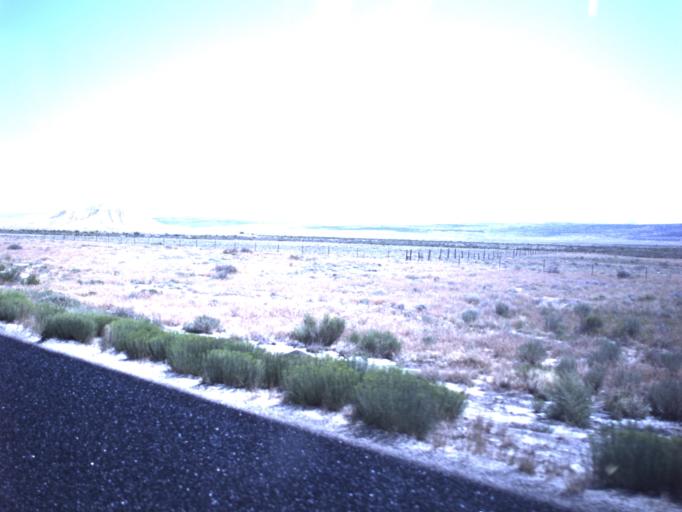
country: US
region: Utah
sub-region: Emery County
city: Ferron
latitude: 39.0065
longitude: -111.1548
